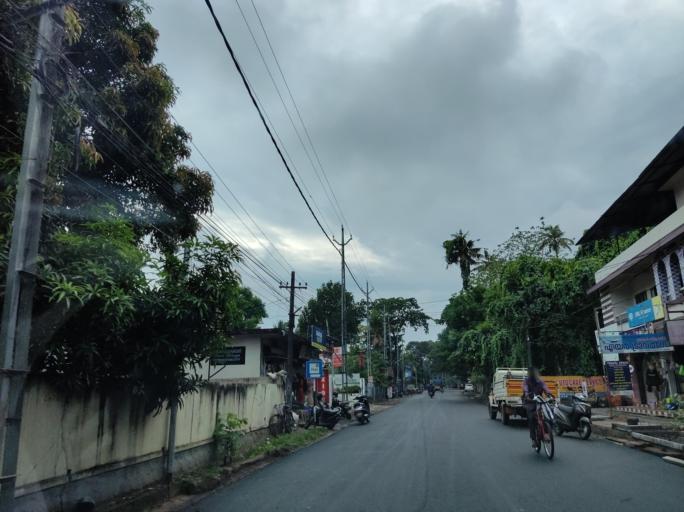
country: IN
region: Kerala
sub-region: Alappuzha
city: Mavelikara
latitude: 9.2508
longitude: 76.5286
